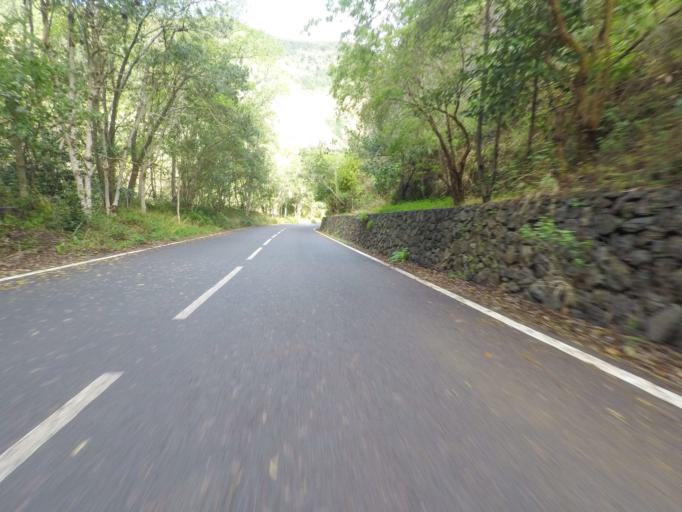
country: ES
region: Canary Islands
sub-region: Provincia de Santa Cruz de Tenerife
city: Hermigua
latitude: 28.1281
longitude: -17.2068
